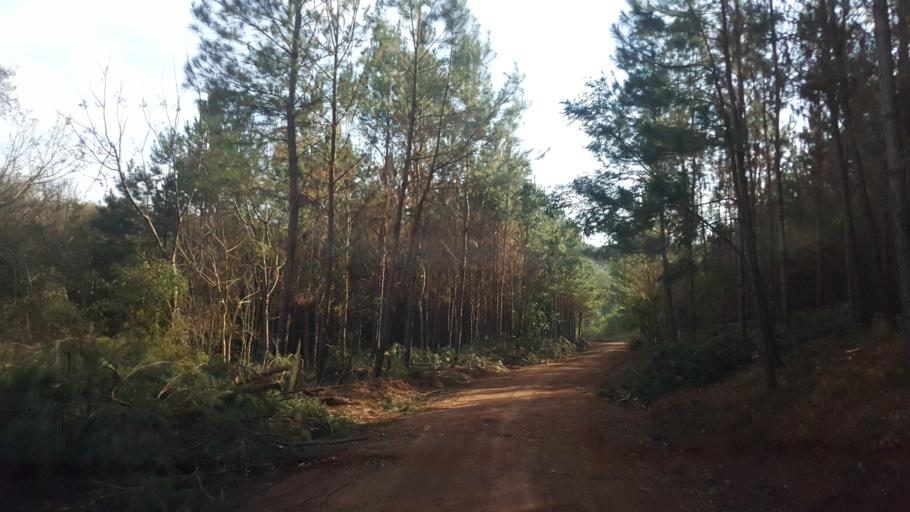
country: AR
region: Misiones
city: Capiovi
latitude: -26.9022
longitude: -55.0922
